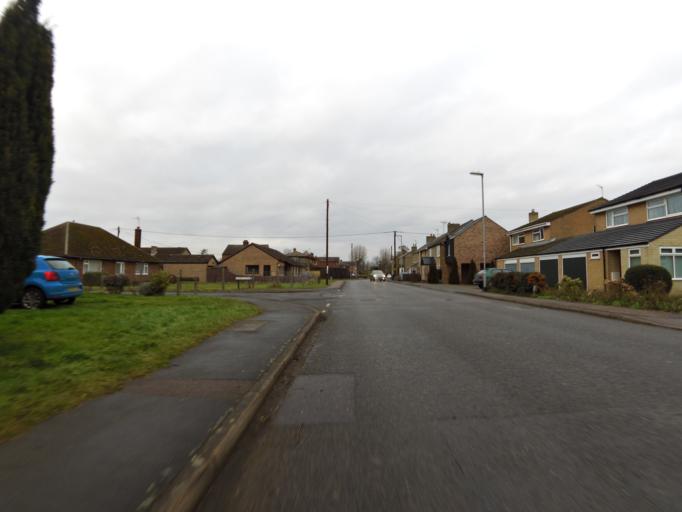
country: GB
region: England
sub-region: Cambridgeshire
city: Waterbeach
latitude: 52.2671
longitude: 0.1934
